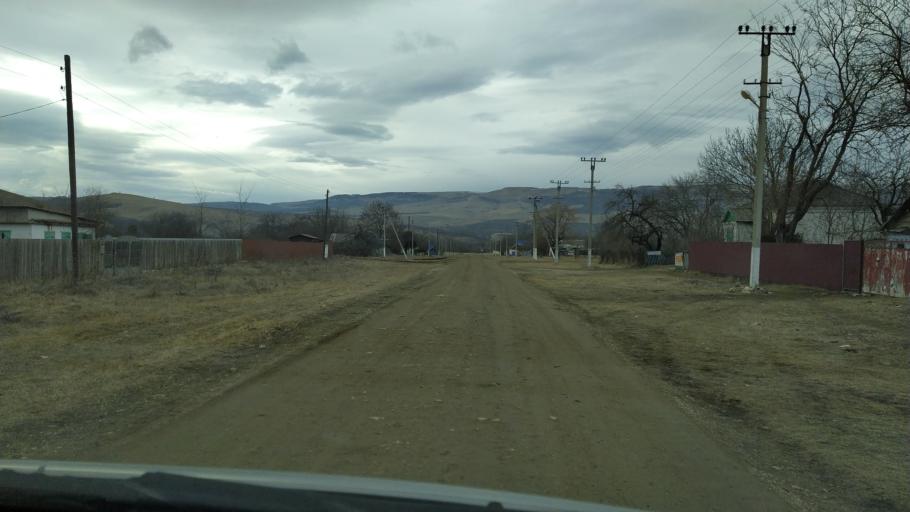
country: RU
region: Krasnodarskiy
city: Peredovaya
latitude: 44.0823
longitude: 41.3689
